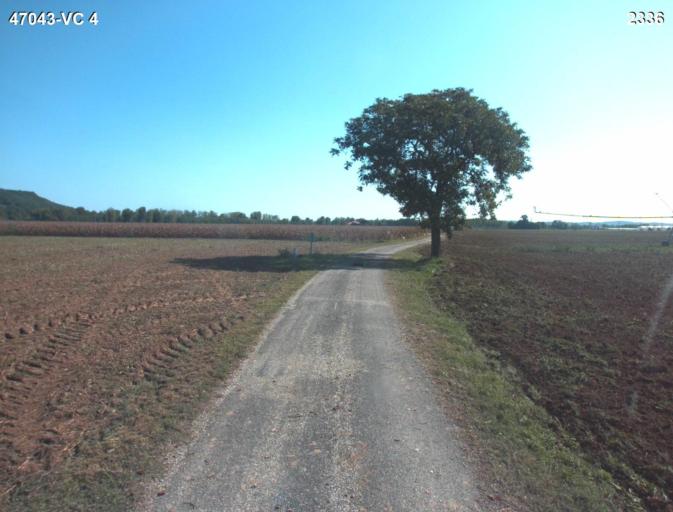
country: FR
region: Aquitaine
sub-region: Departement du Lot-et-Garonne
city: Buzet-sur-Baise
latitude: 44.2705
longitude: 0.3264
